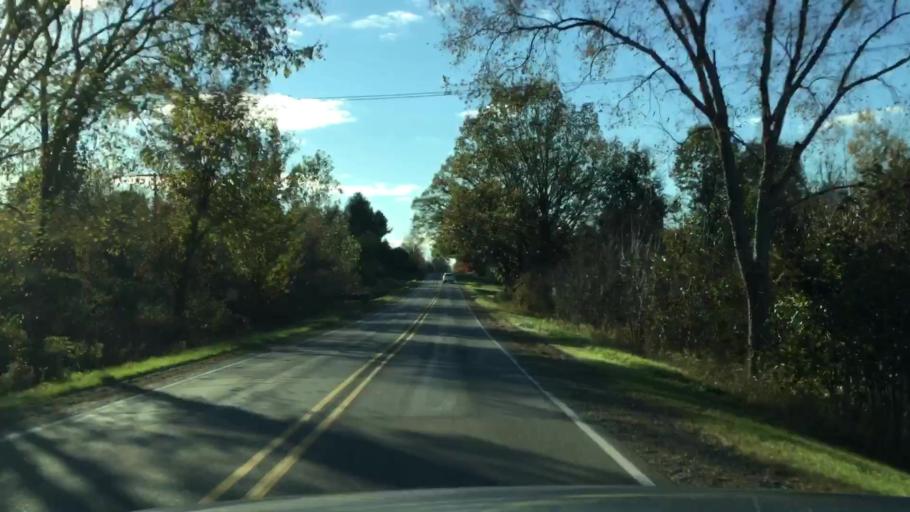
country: US
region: Michigan
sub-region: Lapeer County
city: Imlay City
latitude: 43.0033
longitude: -83.1688
